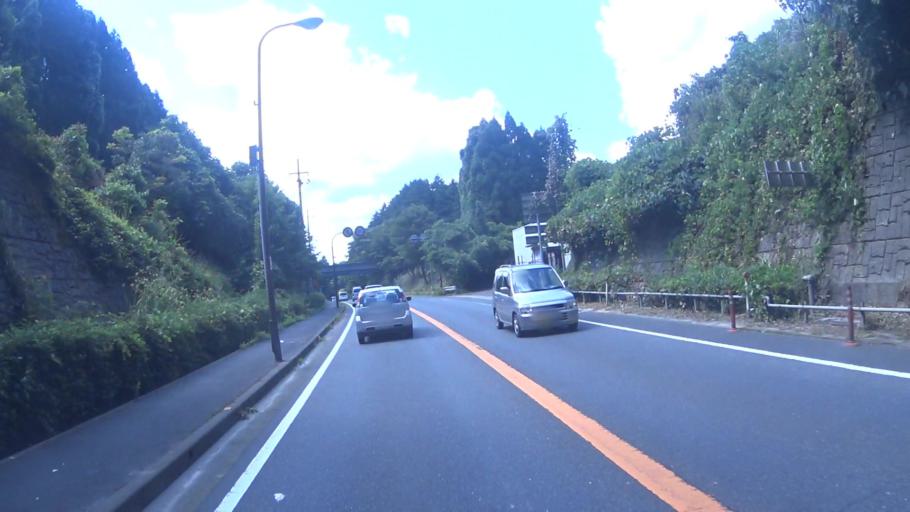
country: JP
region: Kyoto
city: Miyazu
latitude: 35.5506
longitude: 135.1716
